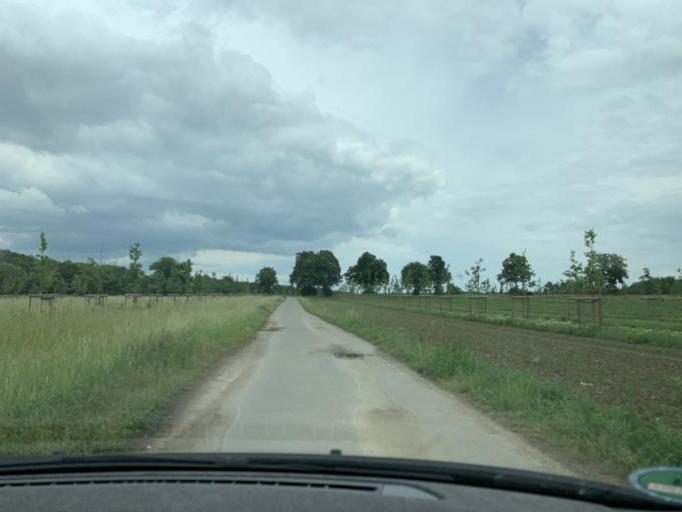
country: DE
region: North Rhine-Westphalia
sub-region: Regierungsbezirk Koln
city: Niederzier
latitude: 50.8926
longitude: 6.4688
